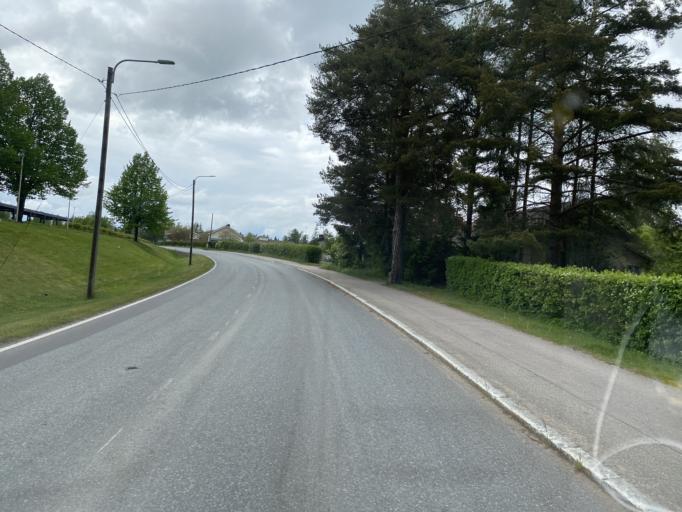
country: FI
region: Pirkanmaa
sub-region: Etelae-Pirkanmaa
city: Urjala
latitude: 61.0799
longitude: 23.5630
